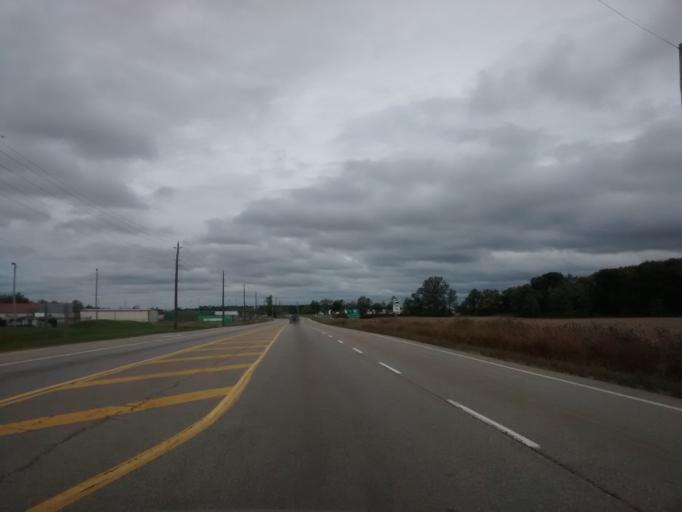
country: CA
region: Ontario
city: Ancaster
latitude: 43.0914
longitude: -79.9521
